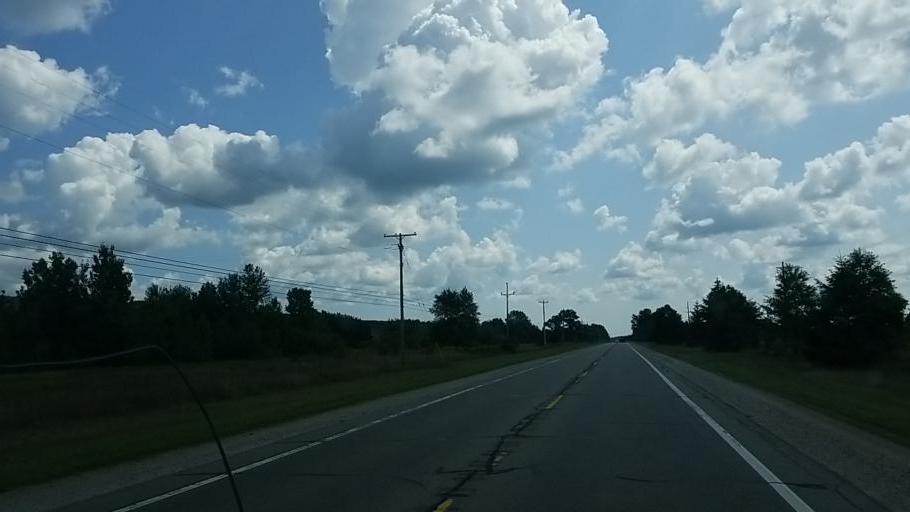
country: US
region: Michigan
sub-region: Muskegon County
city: Wolf Lake
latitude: 43.2352
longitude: -86.0208
